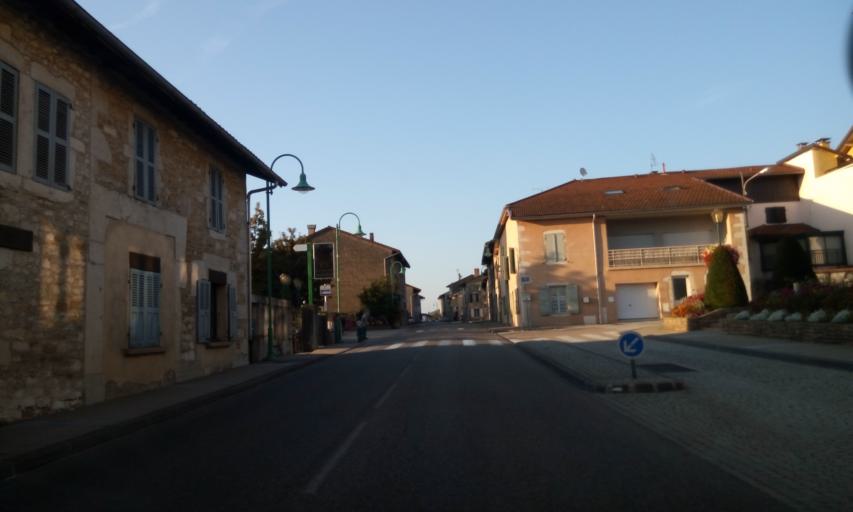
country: FR
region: Rhone-Alpes
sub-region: Departement de l'Ain
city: Saint-Martin-du-Frene
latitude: 46.1399
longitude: 5.5530
